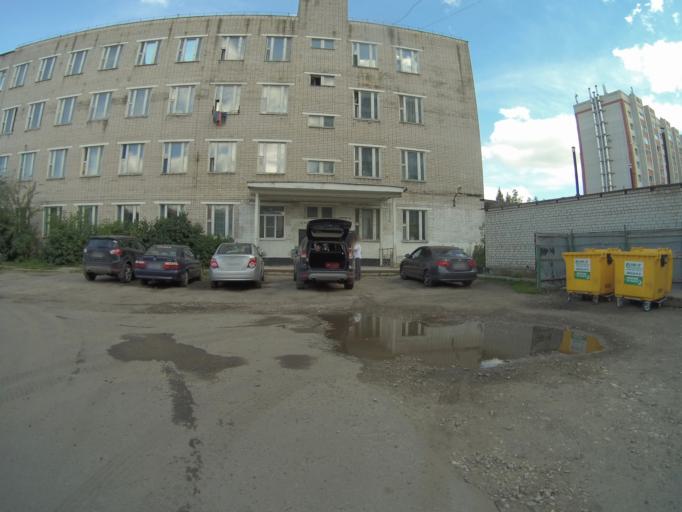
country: RU
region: Vladimir
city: Vladimir
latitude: 56.1359
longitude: 40.3653
